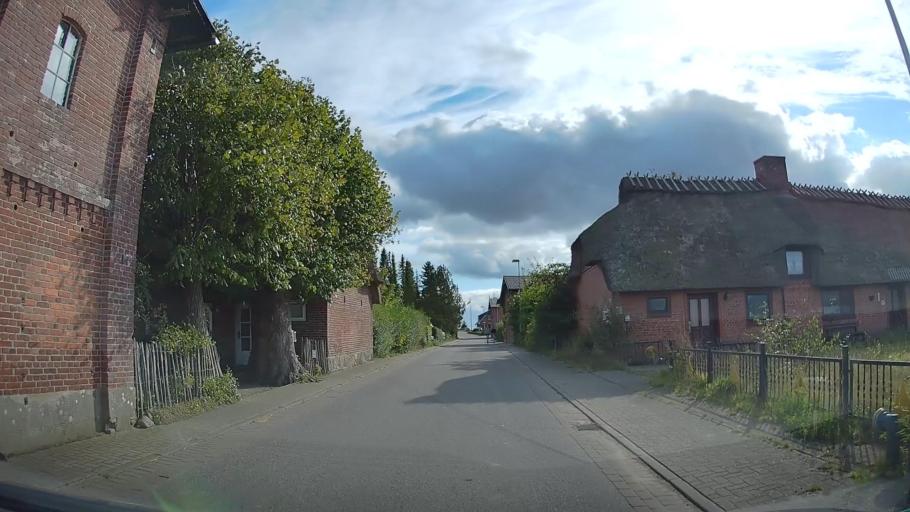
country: DE
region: Schleswig-Holstein
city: Steinberg
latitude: 54.8000
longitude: 9.7557
